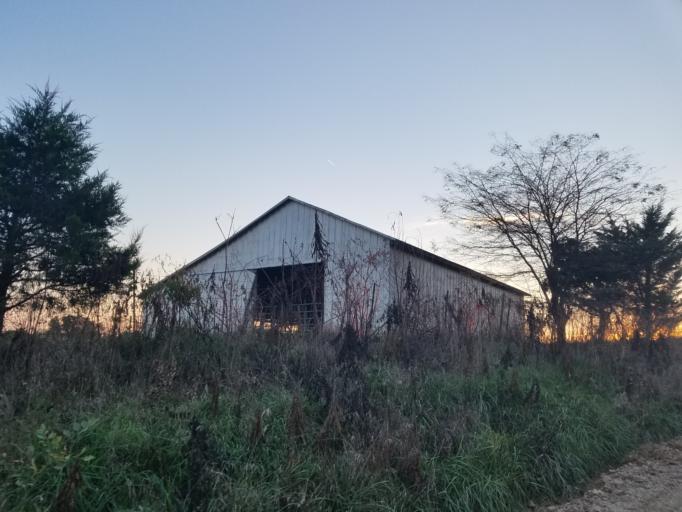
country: US
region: Missouri
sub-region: Moniteau County
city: California
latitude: 38.7477
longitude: -92.6341
